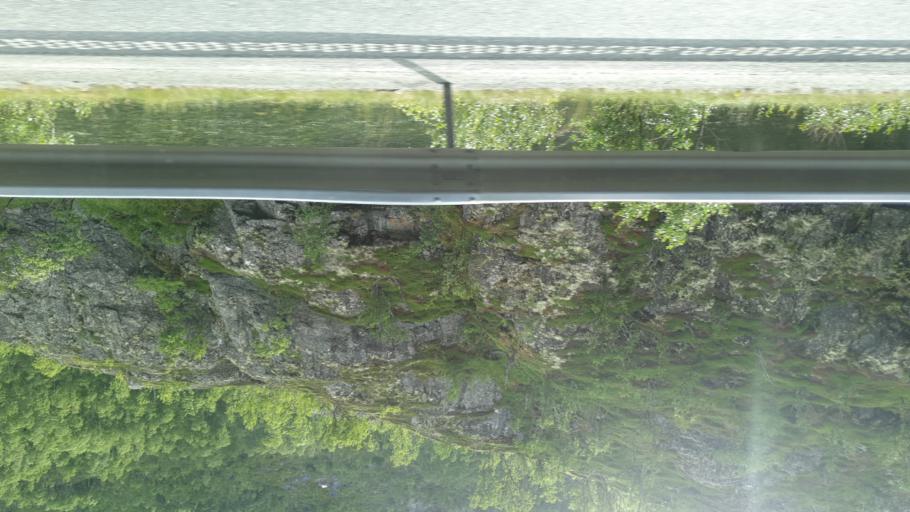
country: NO
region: Sor-Trondelag
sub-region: Oppdal
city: Oppdal
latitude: 62.3652
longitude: 9.6363
